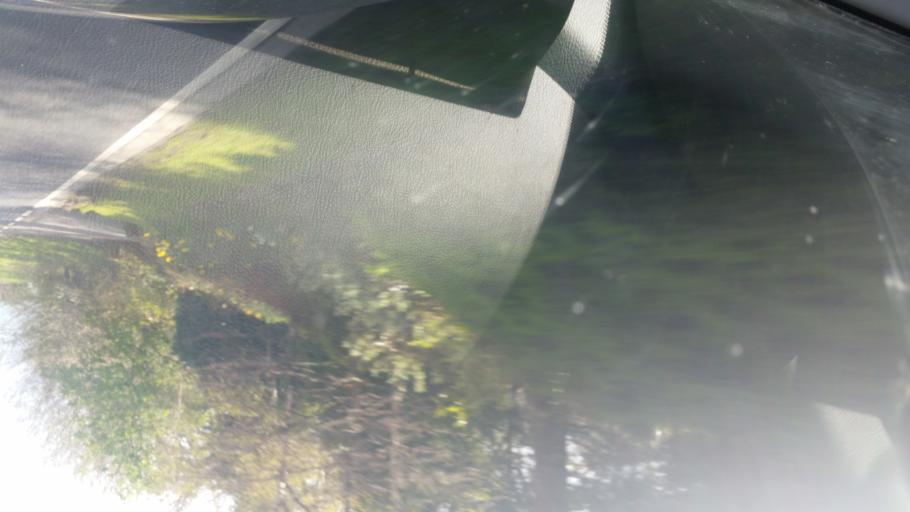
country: GB
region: Northern Ireland
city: Irvinestown
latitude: 54.4242
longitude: -7.7494
